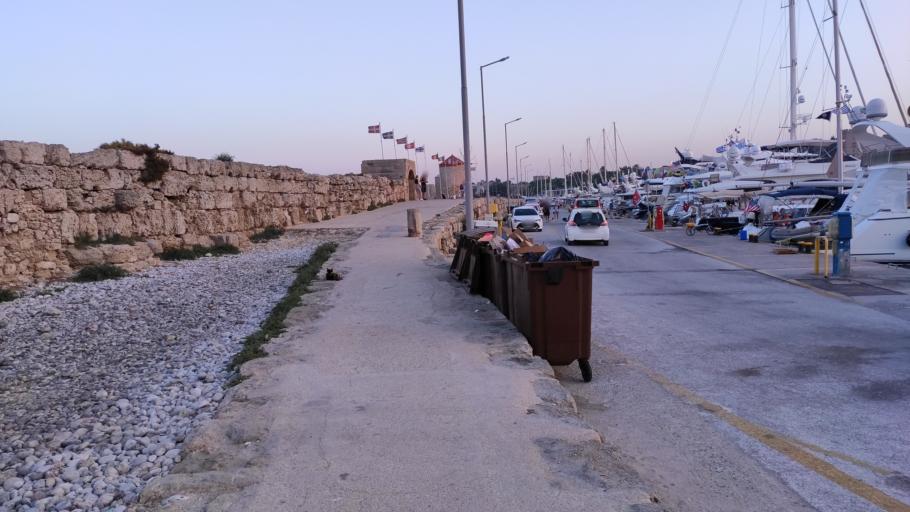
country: GR
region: South Aegean
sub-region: Nomos Dodekanisou
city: Rodos
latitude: 36.4508
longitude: 28.2280
